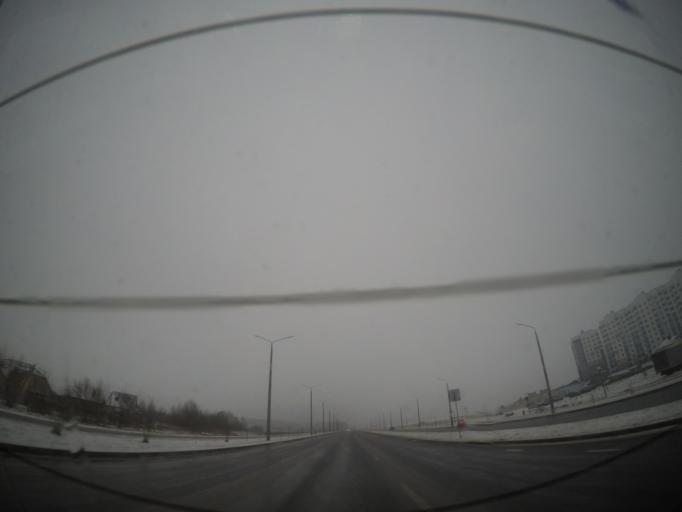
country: BY
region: Grodnenskaya
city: Hrodna
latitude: 53.6140
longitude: 23.8213
